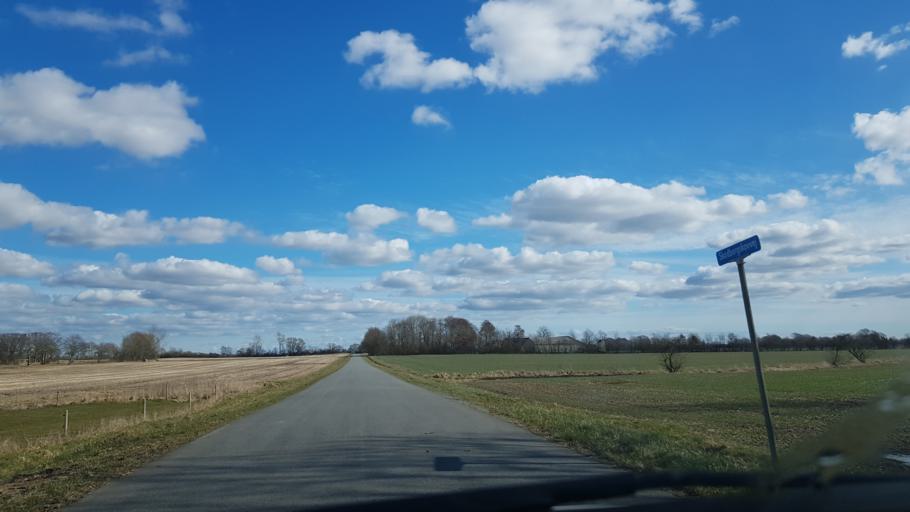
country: DK
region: South Denmark
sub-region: Kolding Kommune
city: Vamdrup
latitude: 55.4095
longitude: 9.2259
